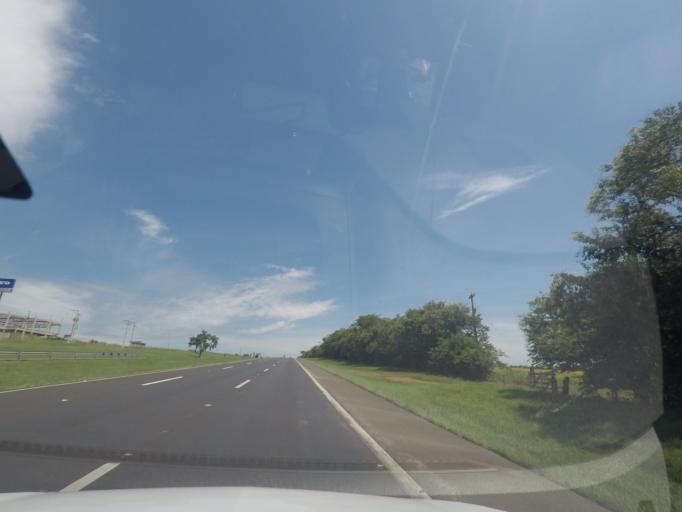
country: BR
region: Sao Paulo
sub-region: Araraquara
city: Araraquara
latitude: -21.7705
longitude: -48.2404
